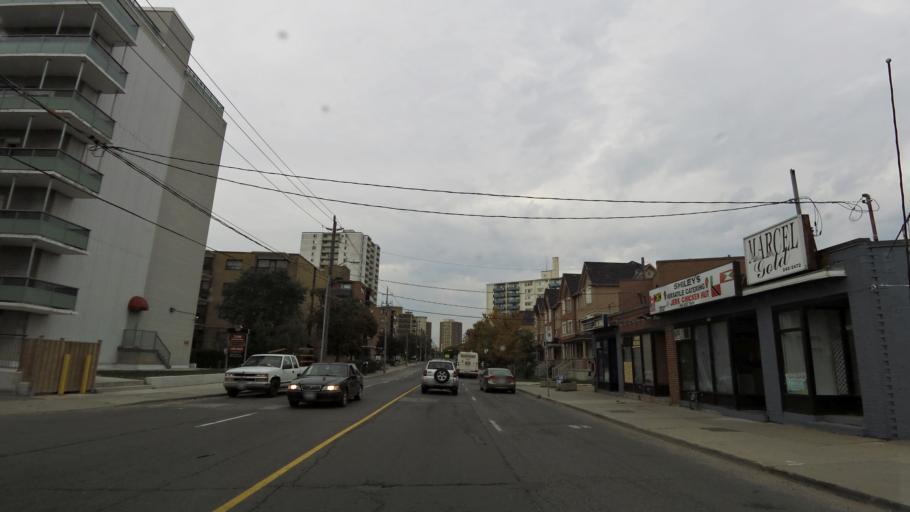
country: CA
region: Ontario
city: Etobicoke
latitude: 43.7032
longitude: -79.5259
